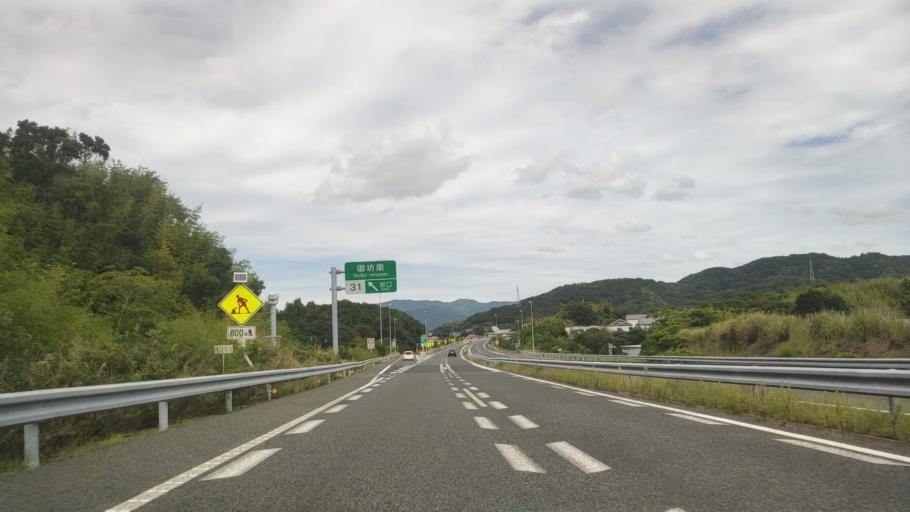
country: JP
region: Wakayama
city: Gobo
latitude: 33.8845
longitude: 135.1827
